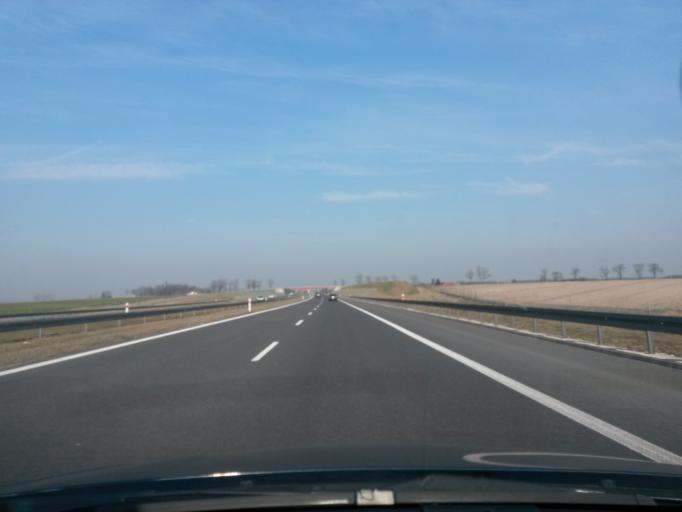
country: PL
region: Lodz Voivodeship
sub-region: Powiat leczycki
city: Piatek
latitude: 52.1214
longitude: 19.4997
